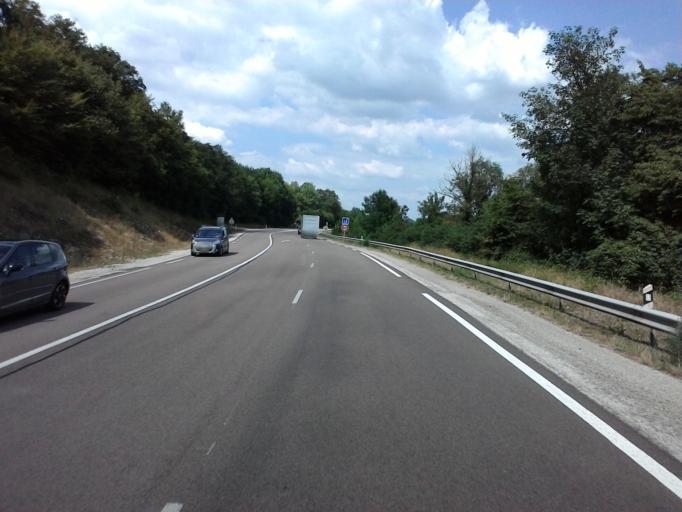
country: FR
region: Franche-Comte
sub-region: Departement du Doubs
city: Avanne-Aveney
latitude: 47.1637
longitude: 5.9549
